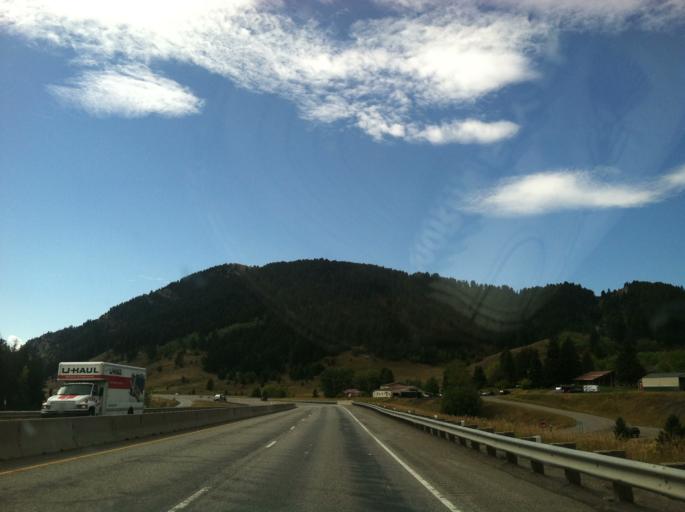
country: US
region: Montana
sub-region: Gallatin County
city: Bozeman
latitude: 45.6468
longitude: -110.8853
